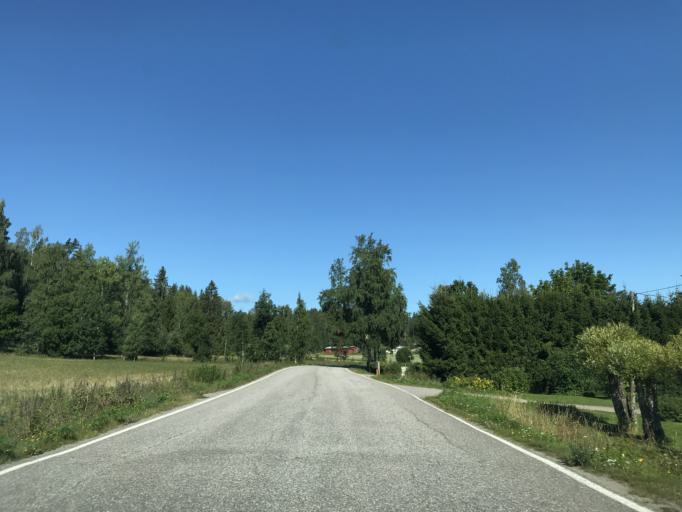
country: FI
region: Paijanne Tavastia
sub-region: Lahti
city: Orimattila
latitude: 60.7997
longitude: 25.6910
